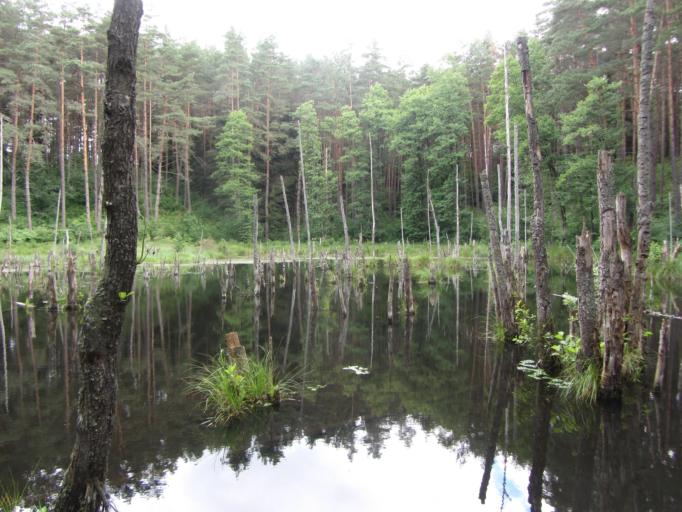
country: LT
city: Grigiskes
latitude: 54.7363
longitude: 25.0382
